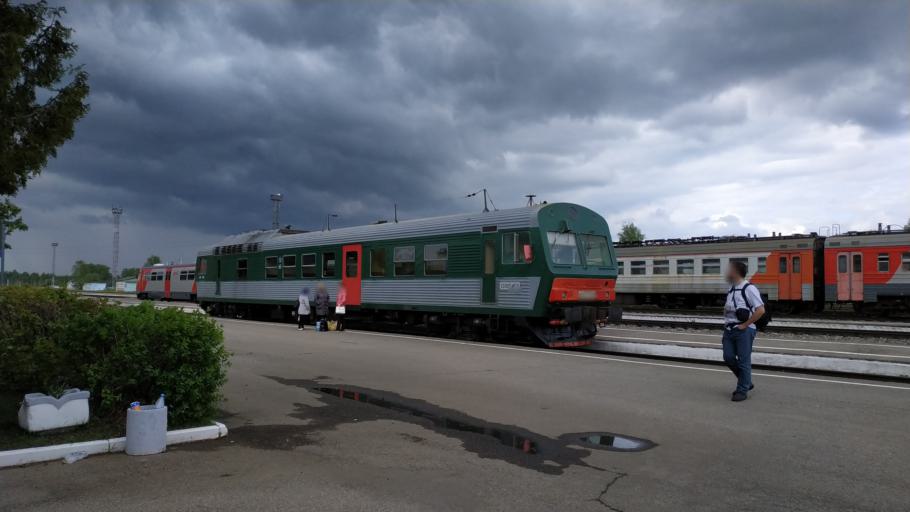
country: RU
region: Kaluga
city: Kirov
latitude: 54.0651
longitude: 34.3749
